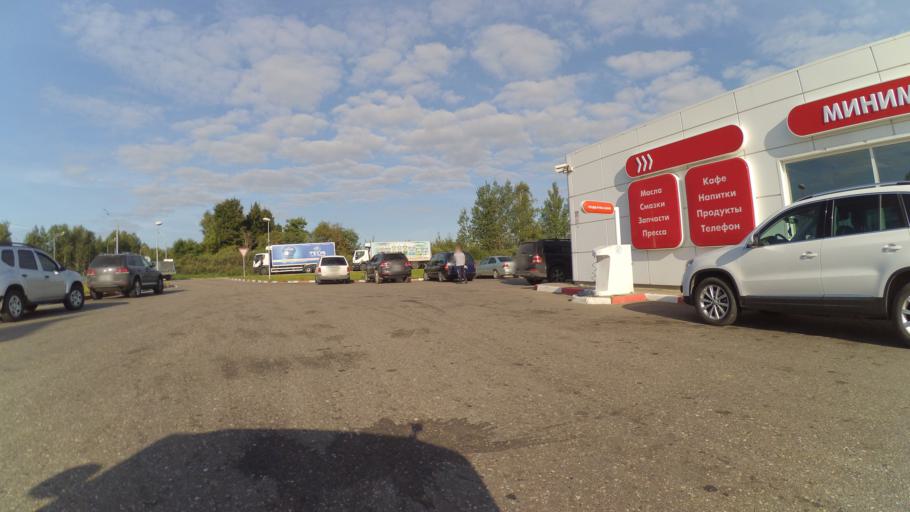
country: RU
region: Moskovskaya
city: Mozhaysk
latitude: 55.4652
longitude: 35.8298
